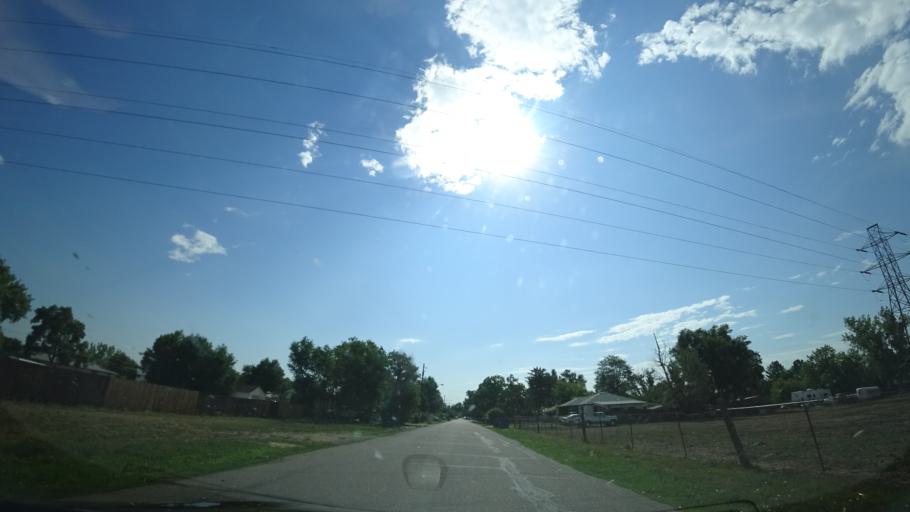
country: US
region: Colorado
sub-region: Jefferson County
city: Lakewood
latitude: 39.7211
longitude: -105.0612
